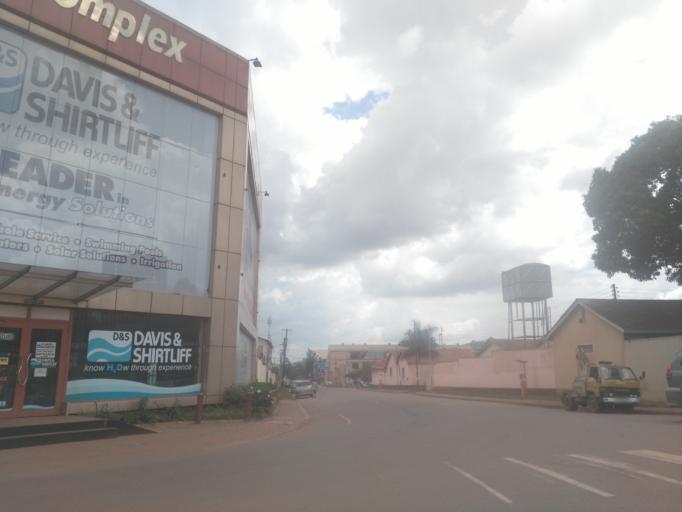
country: UG
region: Central Region
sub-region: Kampala District
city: Kampala
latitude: 0.3238
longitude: 32.6028
